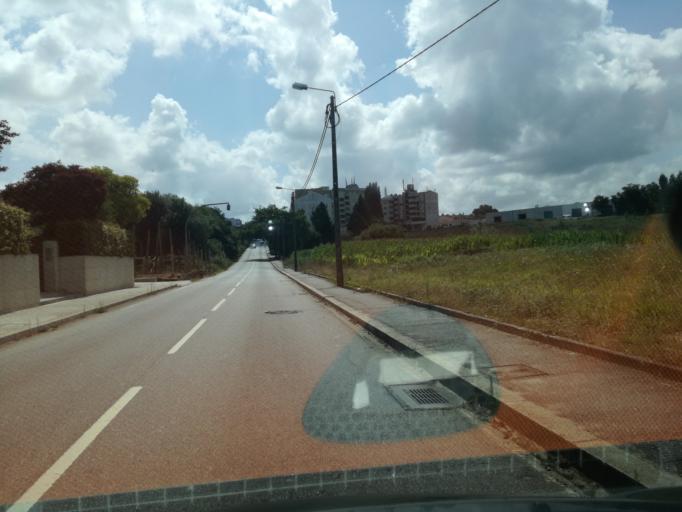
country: PT
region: Porto
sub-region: Maia
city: Nogueira
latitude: 41.2316
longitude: -8.5908
